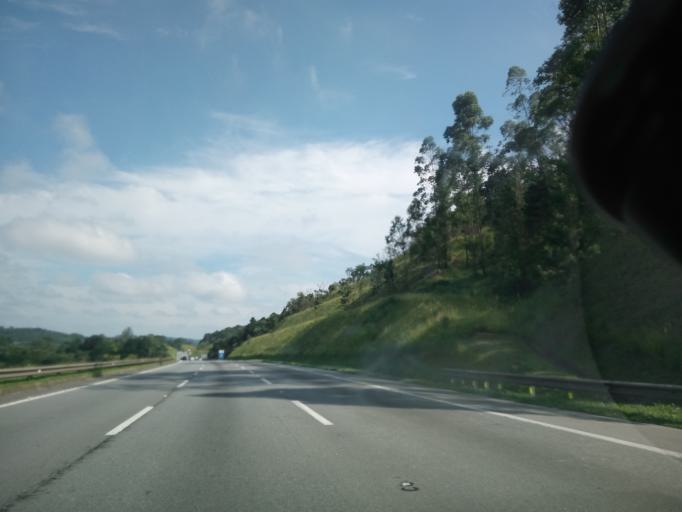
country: BR
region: Sao Paulo
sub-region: Itapecerica Da Serra
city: Itapecerica da Serra
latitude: -23.6818
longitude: -46.8197
